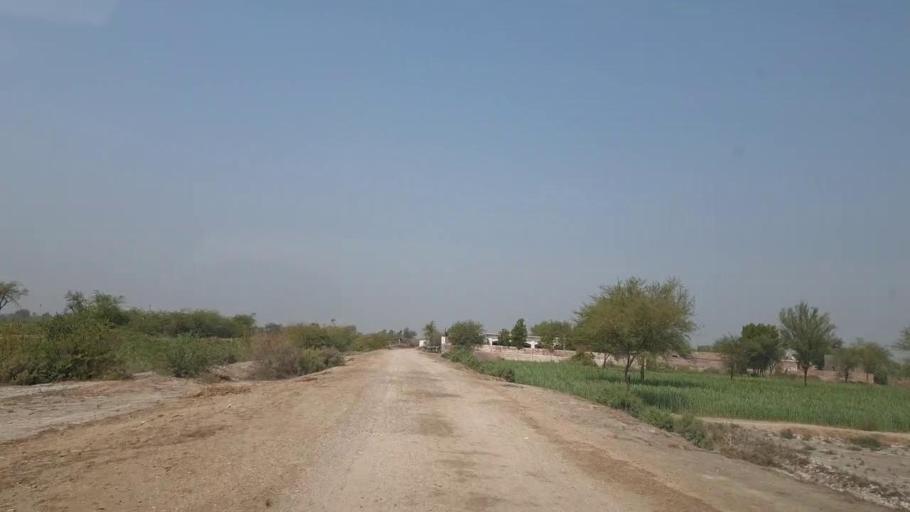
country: PK
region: Sindh
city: Mirpur Khas
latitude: 25.5514
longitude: 69.0763
